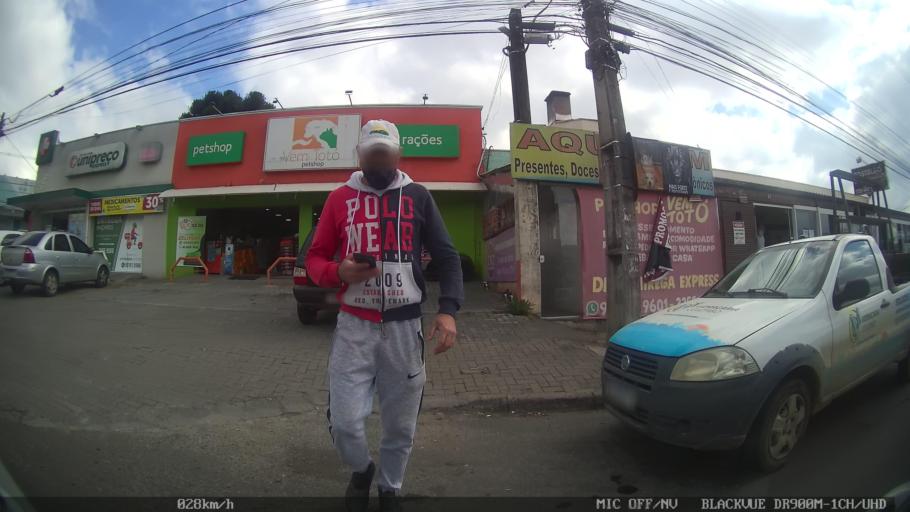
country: BR
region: Parana
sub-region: Pinhais
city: Pinhais
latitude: -25.3753
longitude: -49.2194
